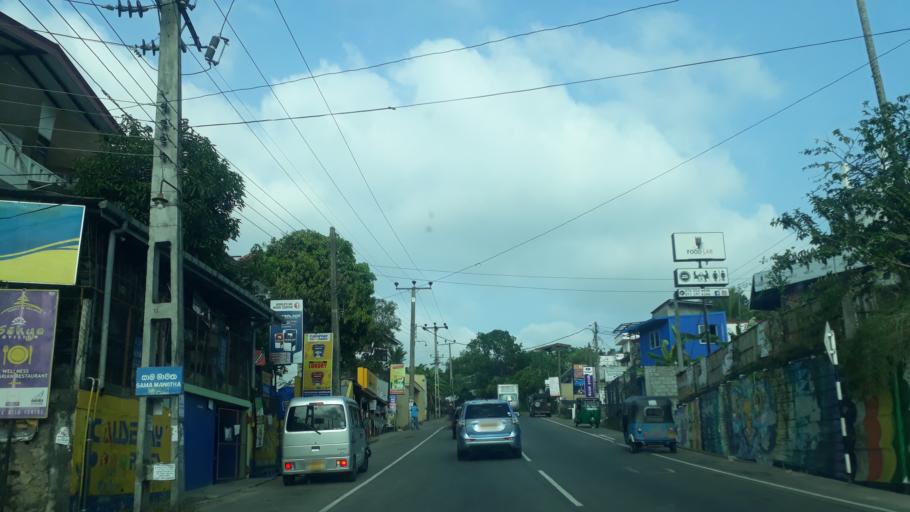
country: LK
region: Western
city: Battaramulla South
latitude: 6.8939
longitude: 79.9397
